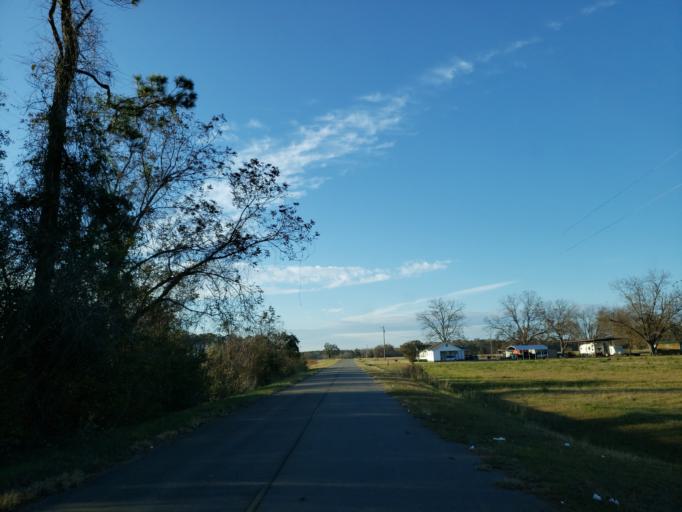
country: US
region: Georgia
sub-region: Dooly County
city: Unadilla
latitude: 32.2083
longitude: -83.7748
